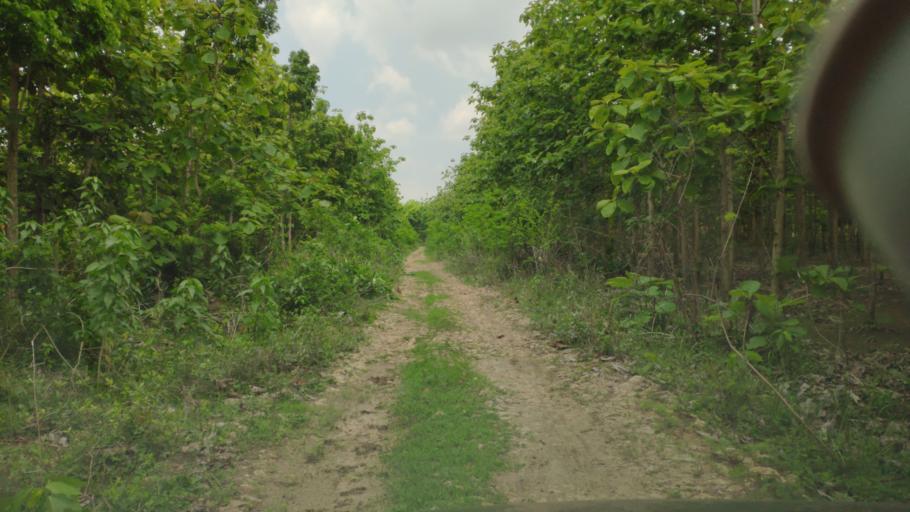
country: ID
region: Central Java
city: Padaan
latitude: -6.9339
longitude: 111.3037
